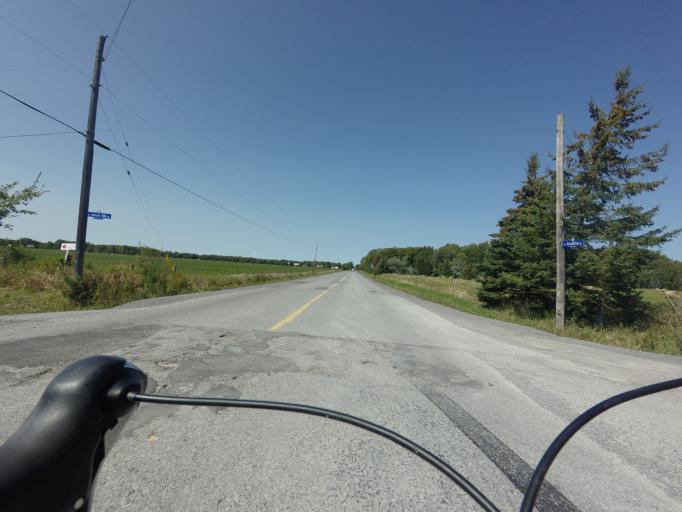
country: CA
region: Ontario
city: Bells Corners
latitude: 45.4338
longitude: -76.0618
